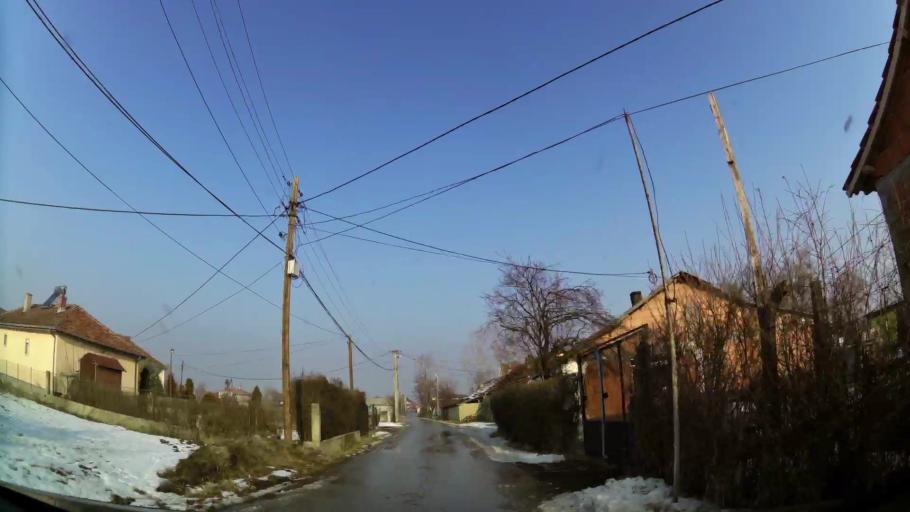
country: MK
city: Kadino
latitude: 41.9664
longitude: 21.5947
